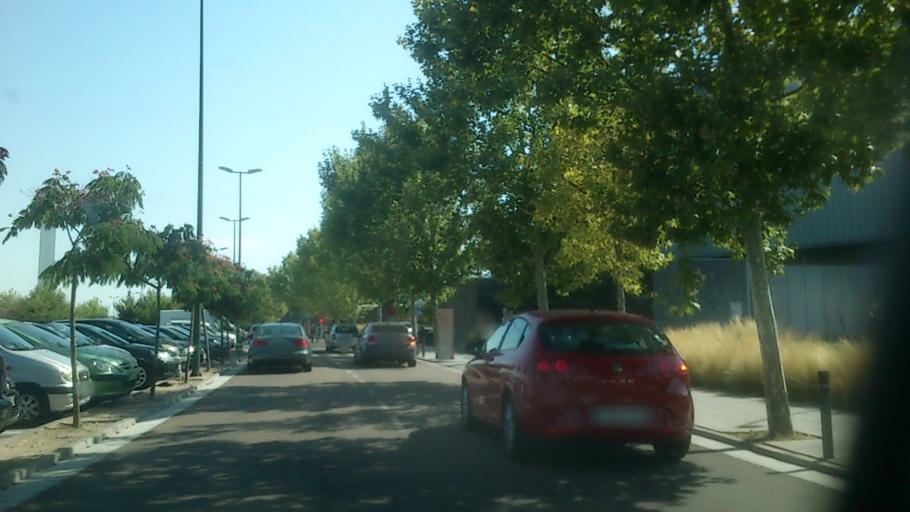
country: ES
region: Aragon
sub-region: Provincia de Zaragoza
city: Delicias
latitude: 41.6096
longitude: -0.8839
